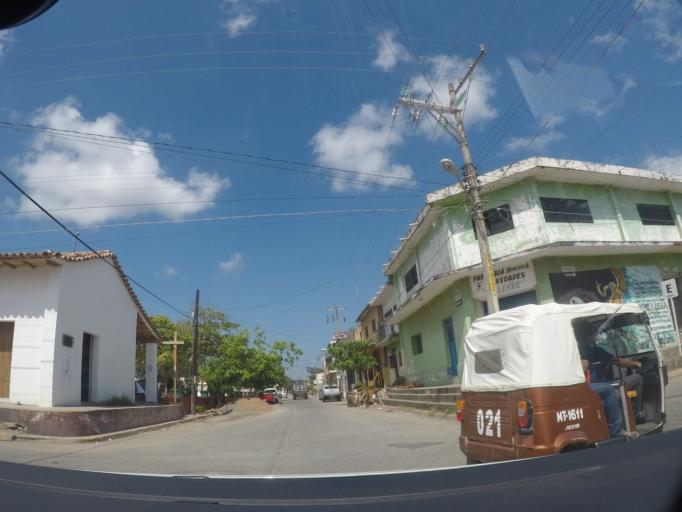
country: MX
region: Oaxaca
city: Juchitan de Zaragoza
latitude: 16.4350
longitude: -95.0177
